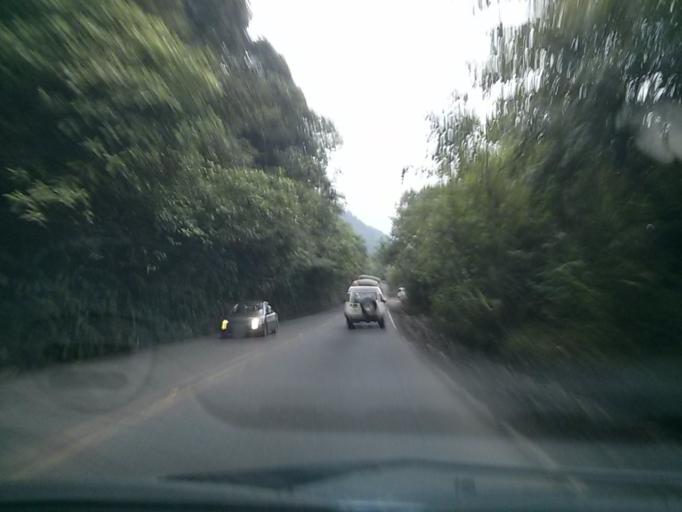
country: CR
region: San Jose
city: Dulce Nombre de Jesus
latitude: 10.1103
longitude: -83.9744
